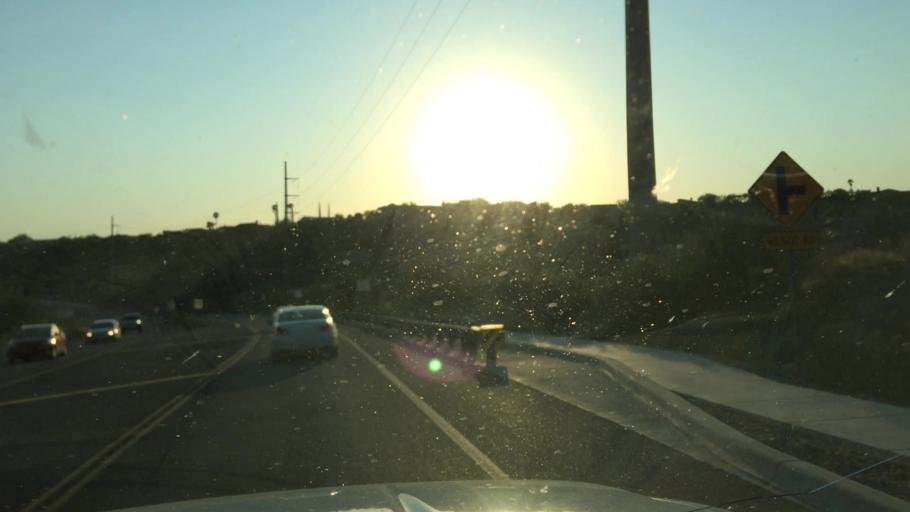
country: US
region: Arizona
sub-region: Pima County
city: Catalina Foothills
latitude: 32.3087
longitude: -110.8581
